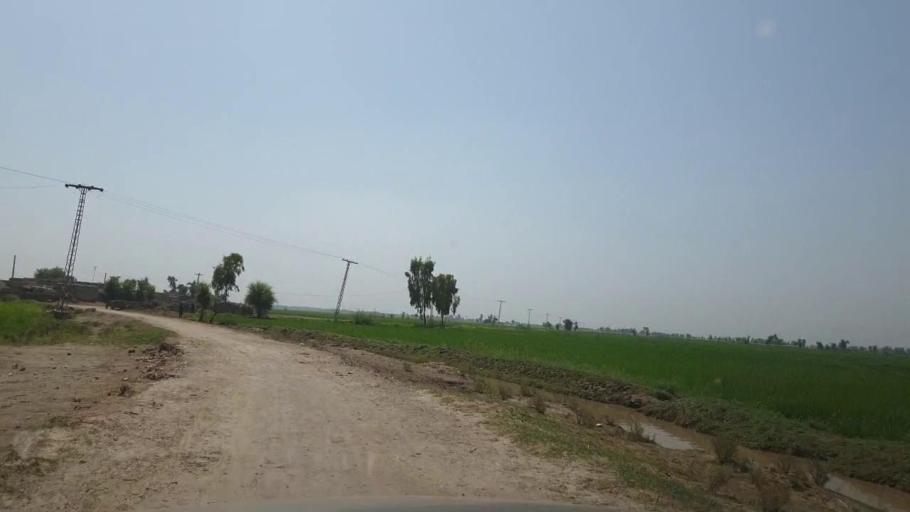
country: PK
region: Sindh
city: Warah
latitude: 27.4849
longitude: 67.7790
